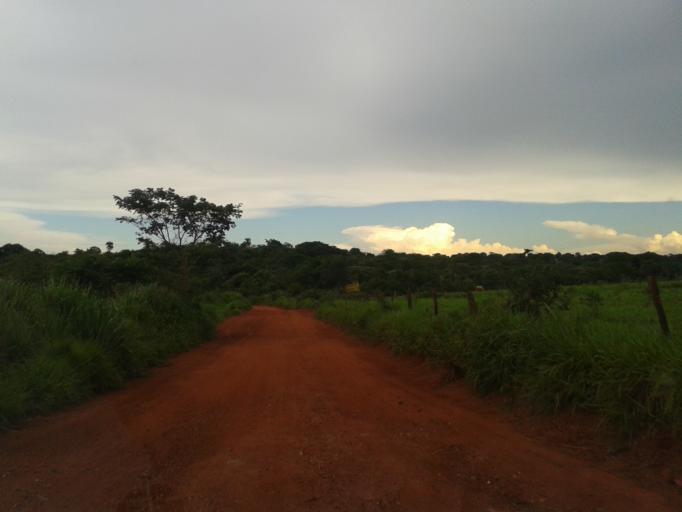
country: BR
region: Minas Gerais
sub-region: Santa Vitoria
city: Santa Vitoria
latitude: -19.1128
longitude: -50.5220
